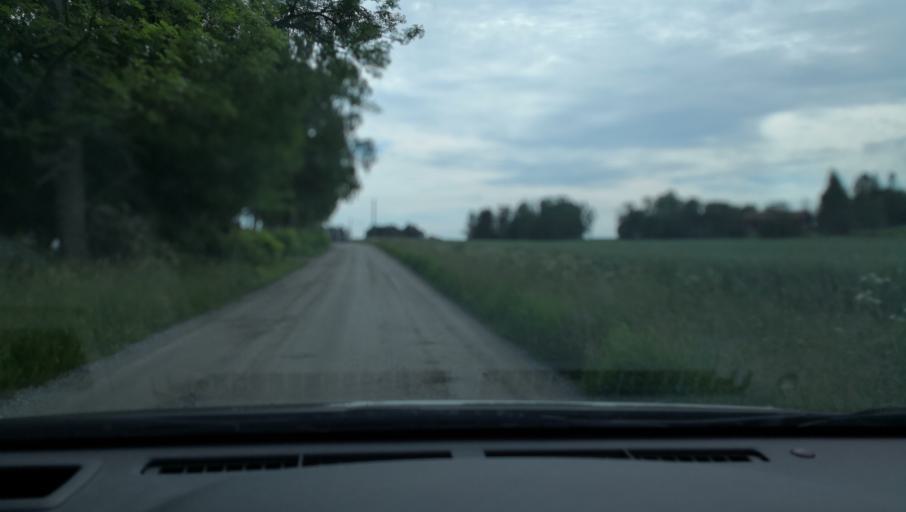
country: SE
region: Uppsala
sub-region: Enkopings Kommun
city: Enkoping
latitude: 59.7038
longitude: 17.1550
